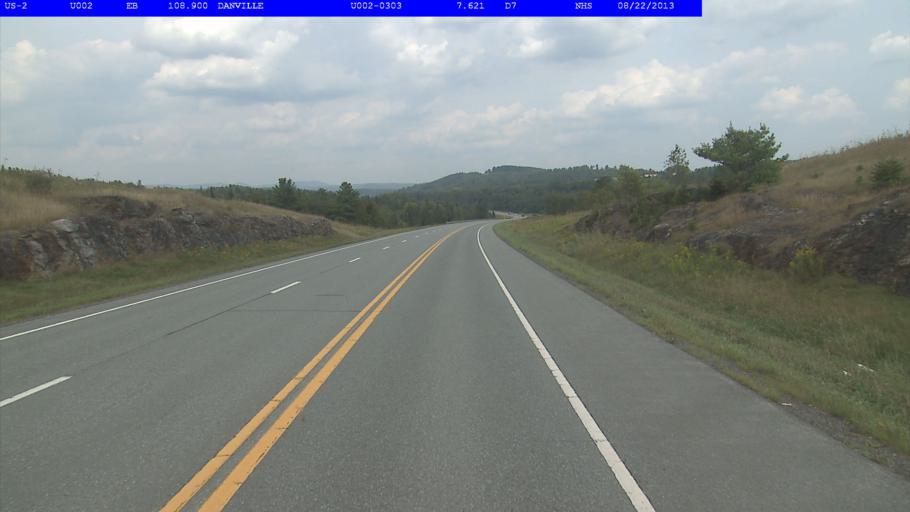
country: US
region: Vermont
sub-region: Caledonia County
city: St Johnsbury
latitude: 44.4338
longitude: -72.0855
